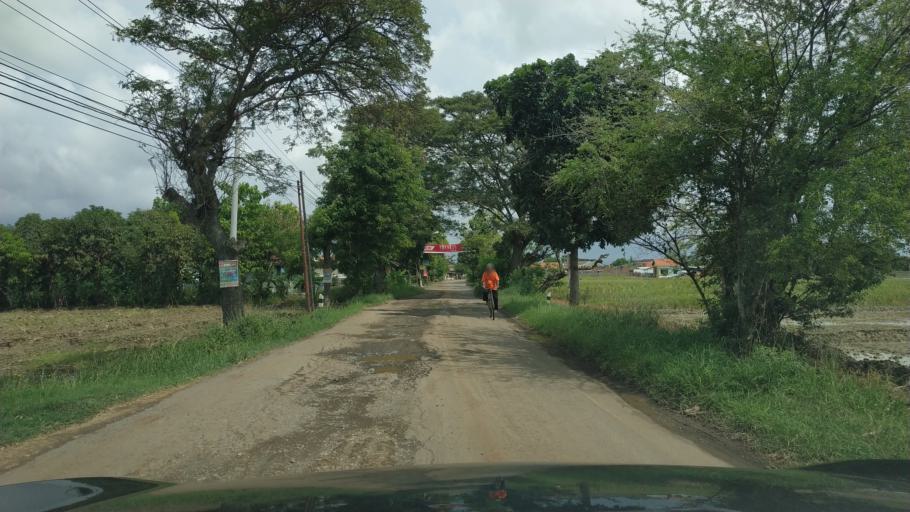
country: ID
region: Central Java
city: Pemalang
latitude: -6.8921
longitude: 109.3274
